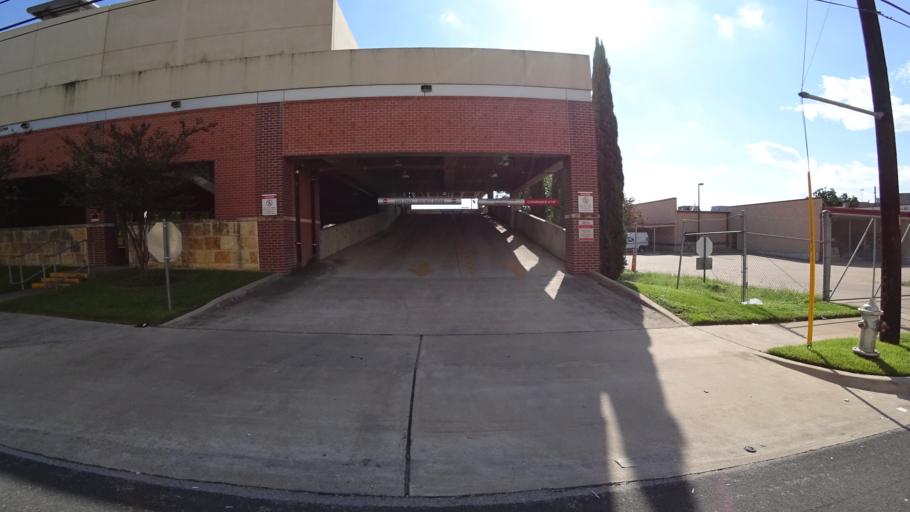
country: US
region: Texas
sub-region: Travis County
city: Austin
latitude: 30.3040
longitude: -97.7427
